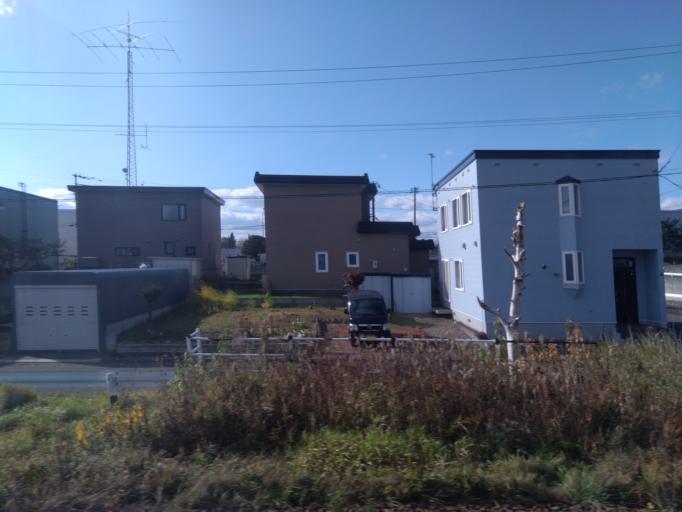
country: JP
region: Hokkaido
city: Kitahiroshima
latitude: 42.9142
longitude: 141.5737
